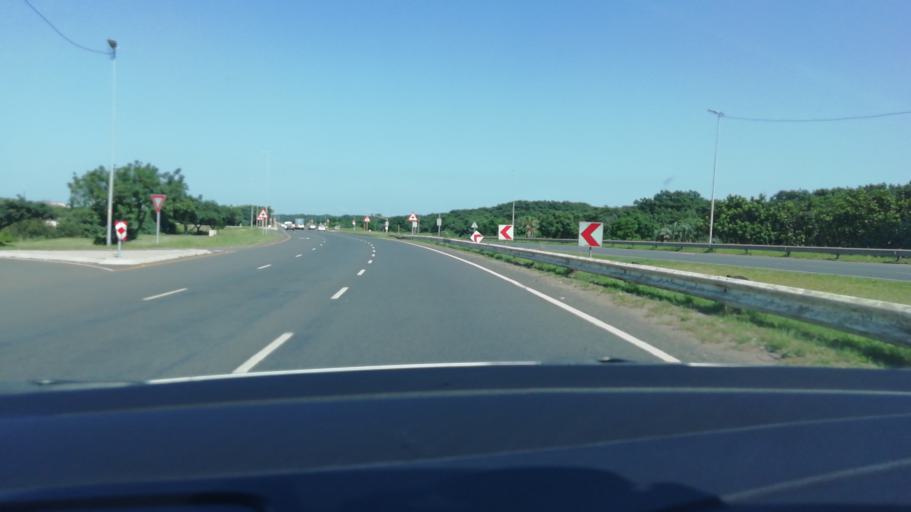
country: ZA
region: KwaZulu-Natal
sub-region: uThungulu District Municipality
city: Richards Bay
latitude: -28.7732
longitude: 32.0709
